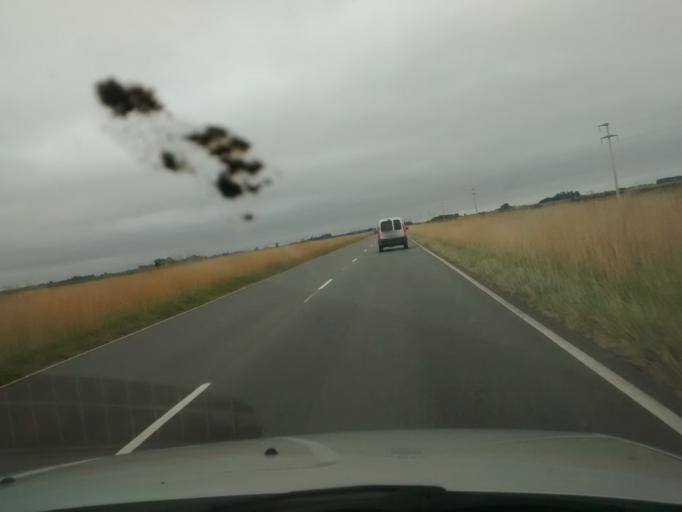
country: AR
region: Buenos Aires
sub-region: Partido de Ayacucho
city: Ayacucho
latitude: -37.0140
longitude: -58.5378
